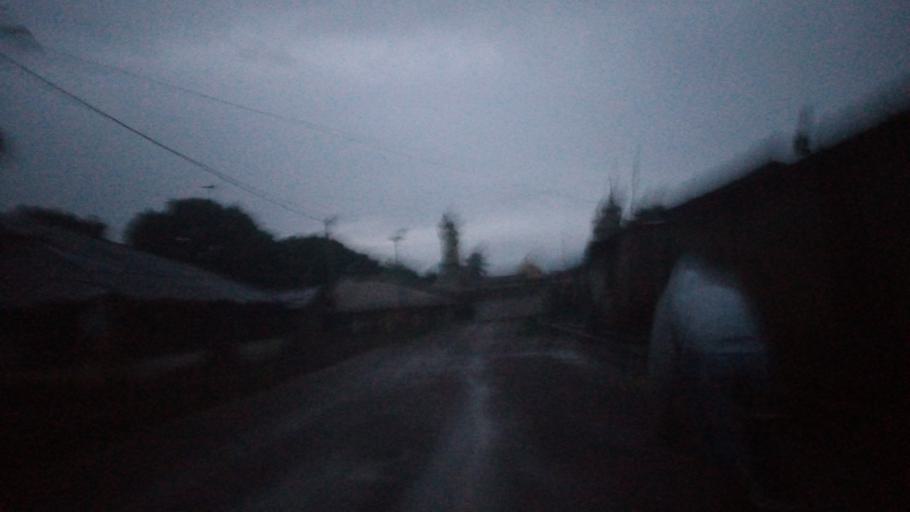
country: SL
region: Northern Province
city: Lunsar
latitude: 8.6863
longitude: -12.5313
